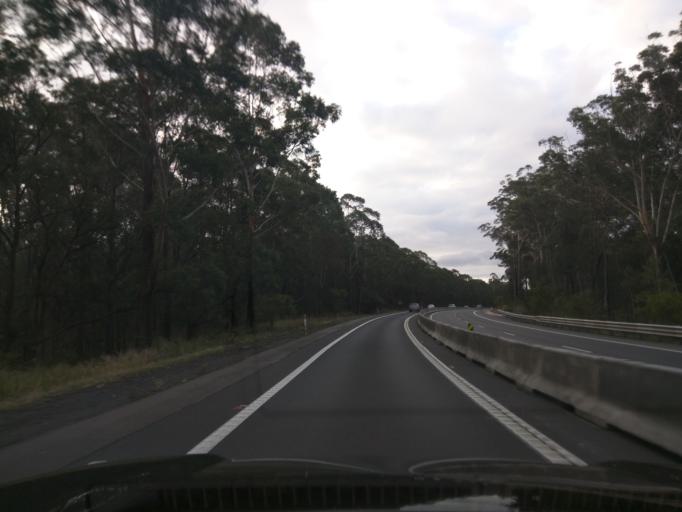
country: AU
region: New South Wales
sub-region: Wollondilly
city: Douglas Park
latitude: -34.2820
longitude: 150.7148
